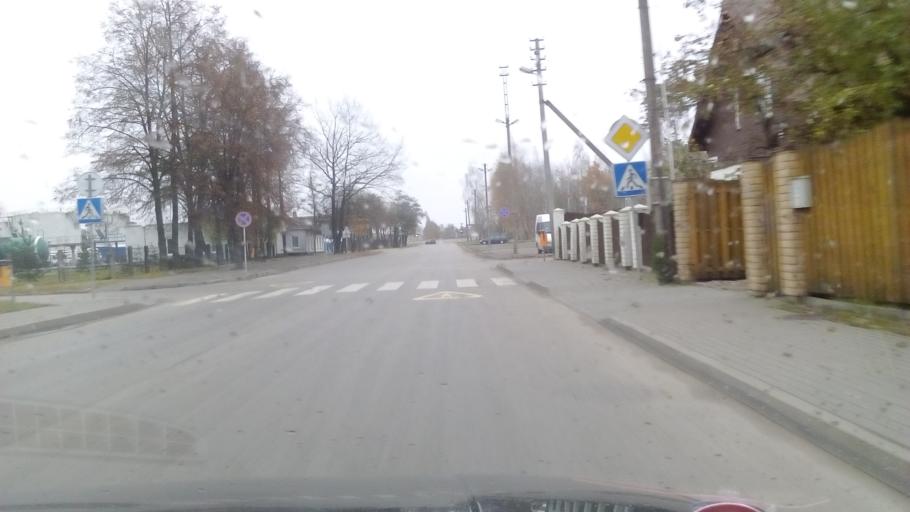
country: LT
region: Marijampoles apskritis
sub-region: Marijampole Municipality
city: Marijampole
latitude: 54.5602
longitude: 23.3612
